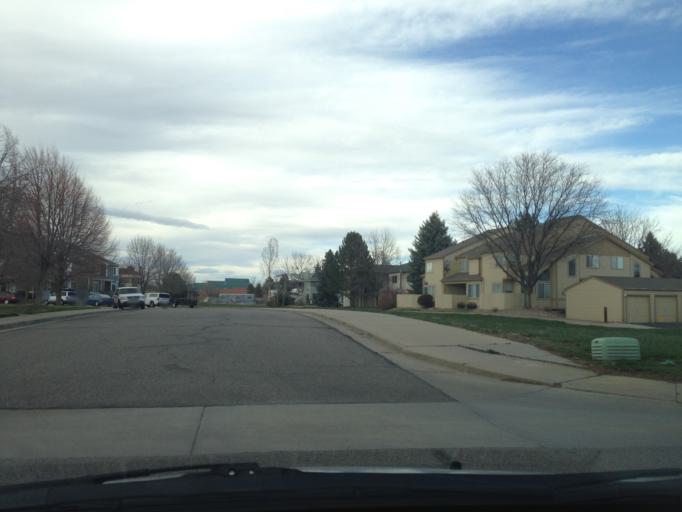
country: US
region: Colorado
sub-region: Boulder County
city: Lafayette
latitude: 39.9845
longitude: -105.1051
